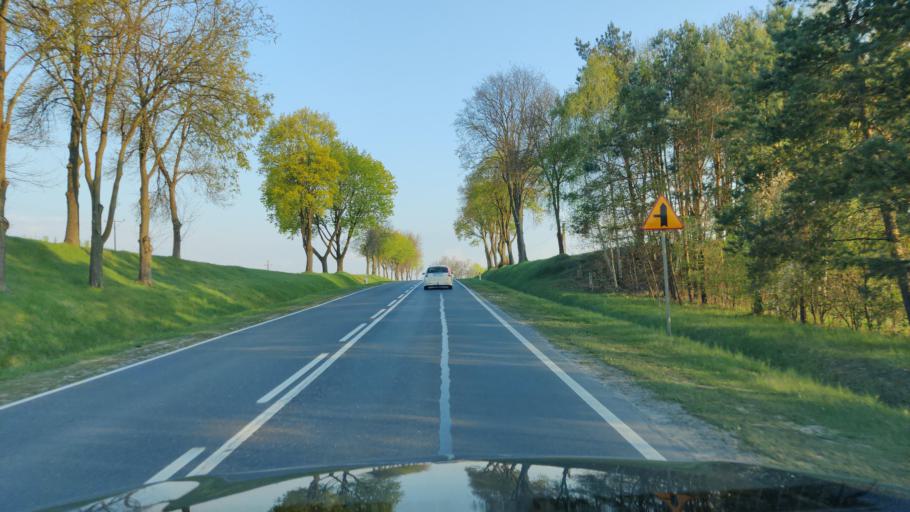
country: PL
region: Masovian Voivodeship
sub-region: Powiat pultuski
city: Zatory
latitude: 52.6011
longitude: 21.1096
